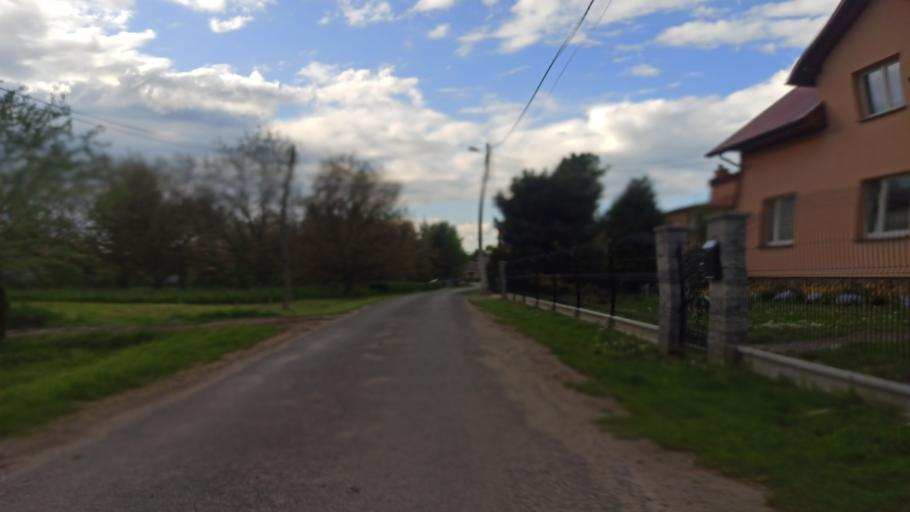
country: PL
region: Subcarpathian Voivodeship
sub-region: Powiat jaroslawski
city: Sosnica
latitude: 49.9210
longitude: 22.8608
